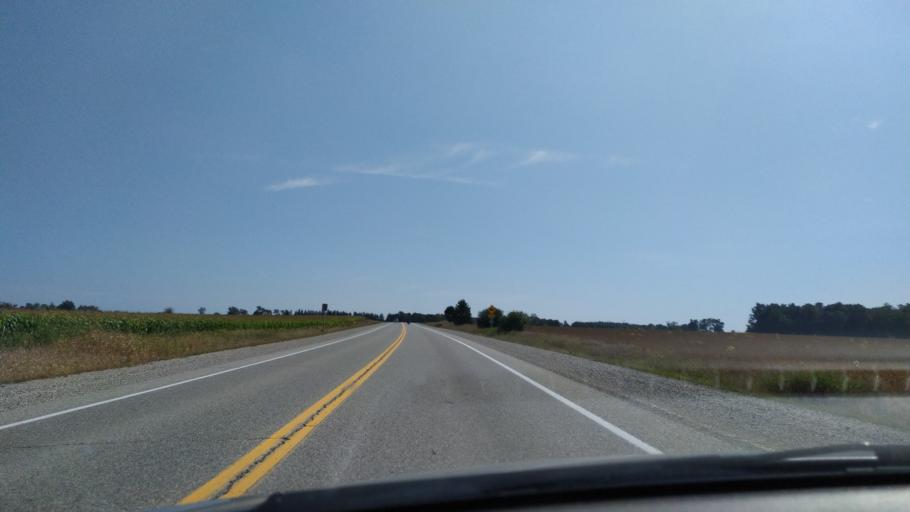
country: CA
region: Ontario
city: Ingersoll
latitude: 43.0935
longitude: -80.8703
